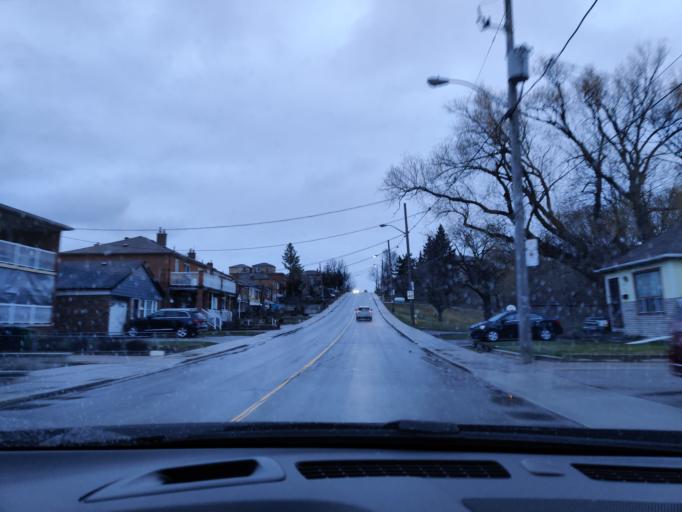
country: CA
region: Ontario
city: Toronto
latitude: 43.6887
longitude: -79.4604
